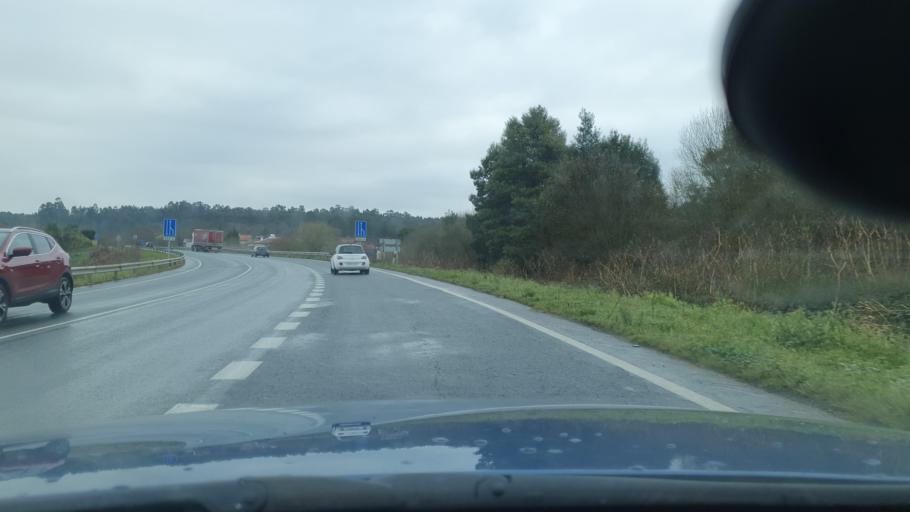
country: ES
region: Galicia
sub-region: Provincia da Coruna
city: Padron
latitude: 42.8088
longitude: -8.6242
